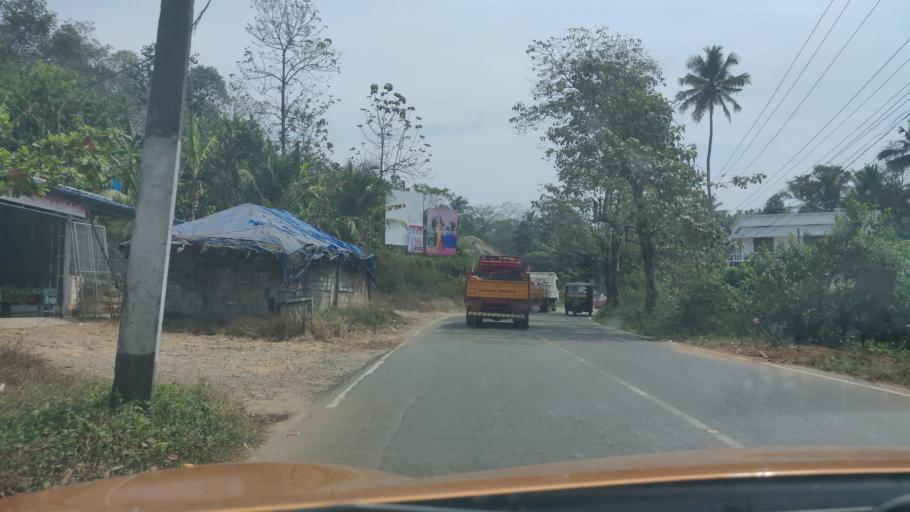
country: IN
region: Kerala
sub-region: Ernakulam
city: Muvattupuzha
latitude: 9.8852
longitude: 76.6481
